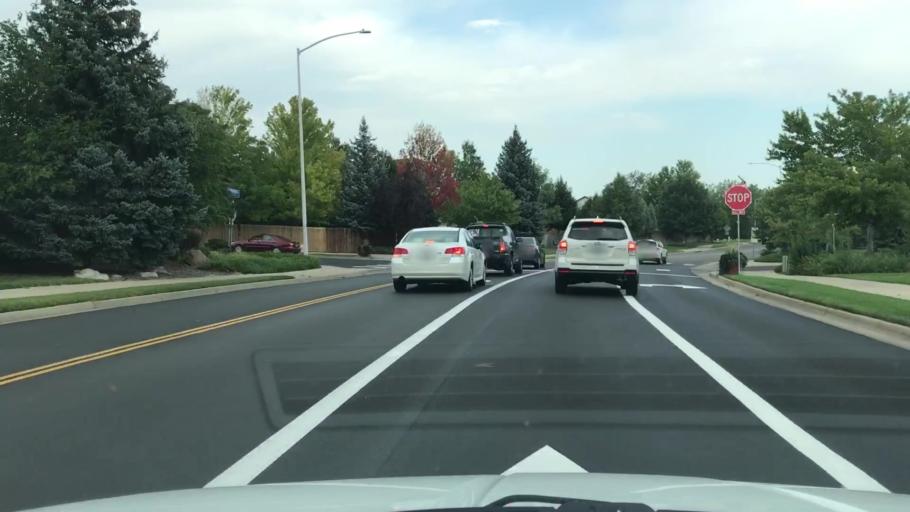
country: US
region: Colorado
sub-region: Broomfield County
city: Broomfield
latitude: 39.9337
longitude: -105.0845
